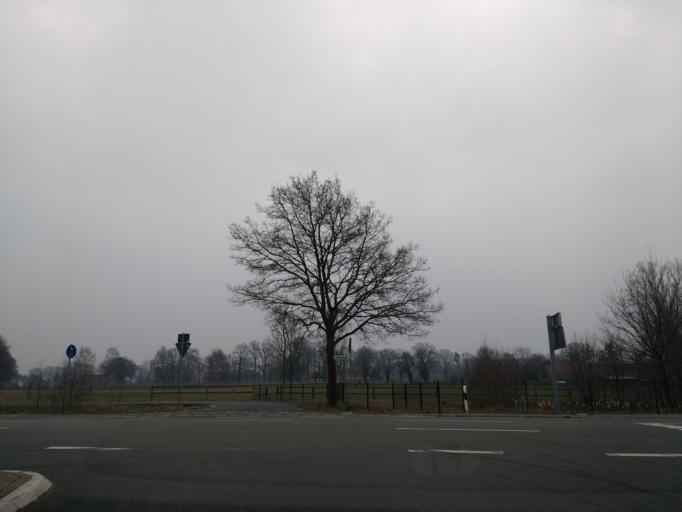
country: DE
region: North Rhine-Westphalia
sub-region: Regierungsbezirk Munster
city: Lotte
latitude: 52.2827
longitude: 7.9236
